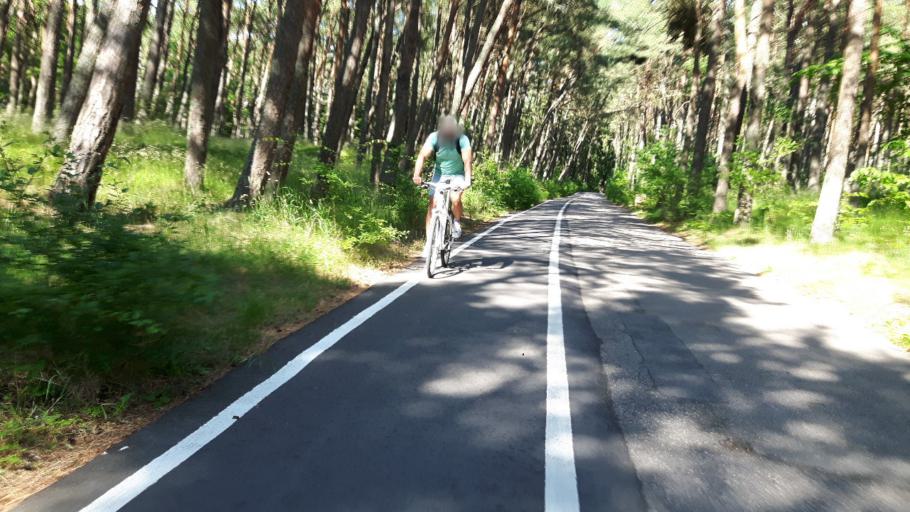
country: LT
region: Klaipedos apskritis
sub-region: Klaipeda
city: Klaipeda
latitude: 55.7008
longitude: 21.1059
